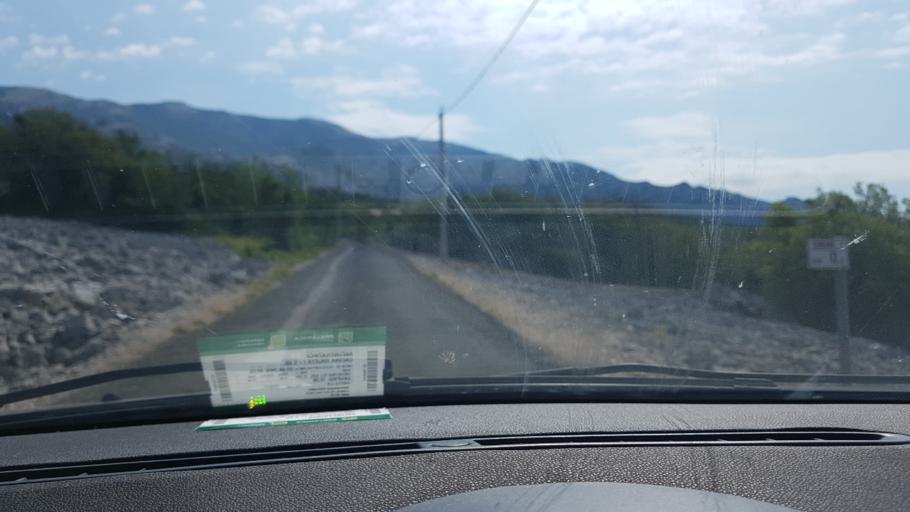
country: HR
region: Primorsko-Goranska
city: Banjol
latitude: 44.6962
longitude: 14.9093
